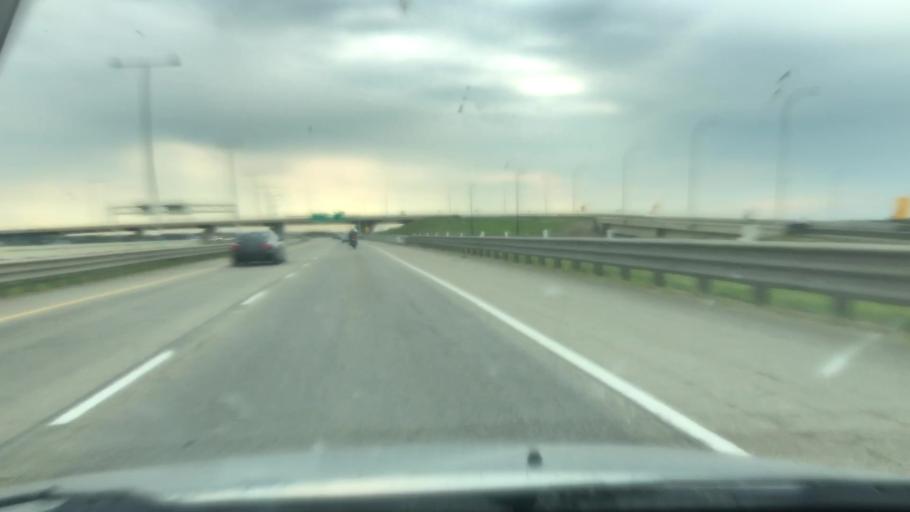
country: CA
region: Alberta
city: Beaumont
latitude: 53.4375
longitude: -113.4884
